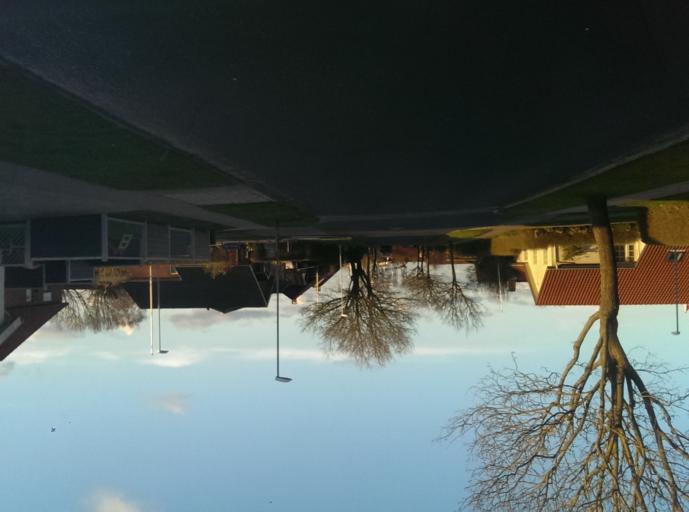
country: DK
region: South Denmark
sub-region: Esbjerg Kommune
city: Esbjerg
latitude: 55.4728
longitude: 8.4768
